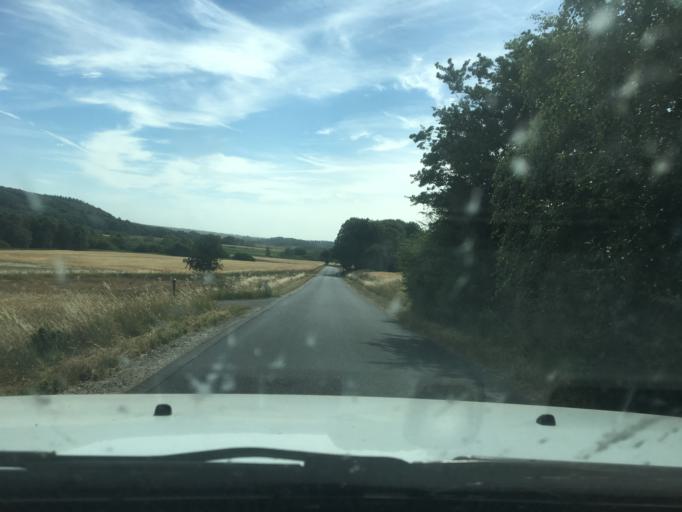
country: DK
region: Central Jutland
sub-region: Viborg Kommune
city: Viborg
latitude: 56.4370
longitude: 9.4747
